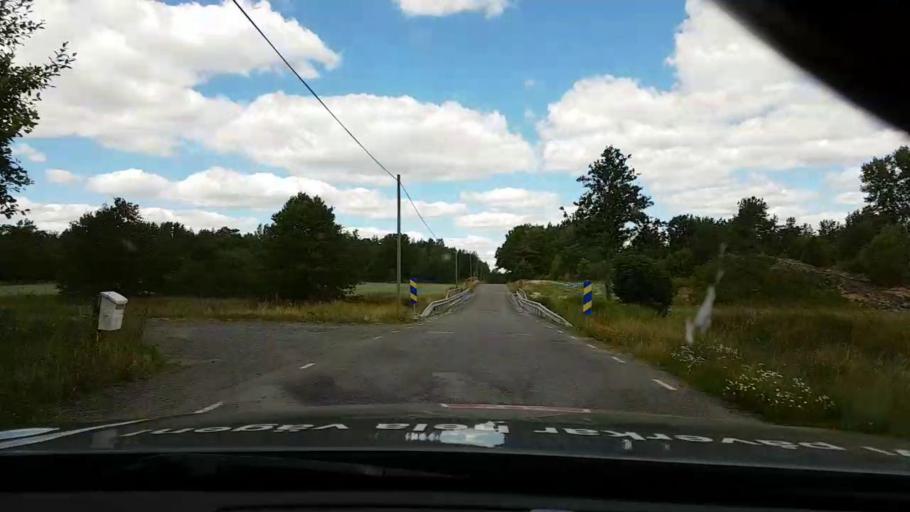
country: SE
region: Kalmar
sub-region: Vasterviks Kommun
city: Forserum
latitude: 57.9931
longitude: 16.6010
